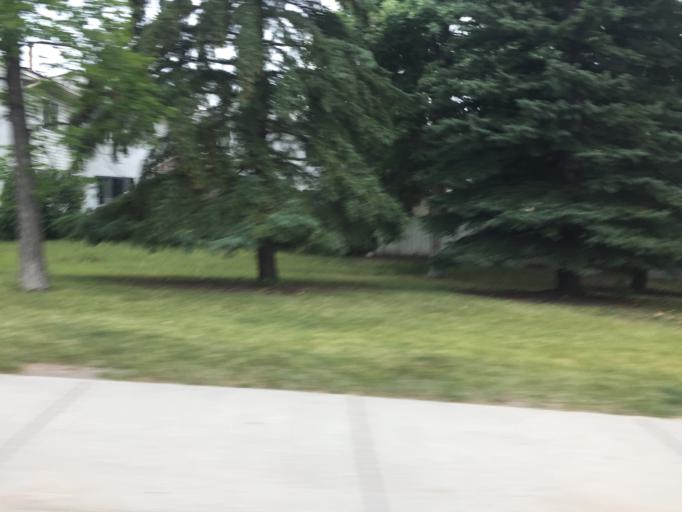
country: CA
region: Alberta
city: Calgary
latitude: 51.0170
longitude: -114.1355
